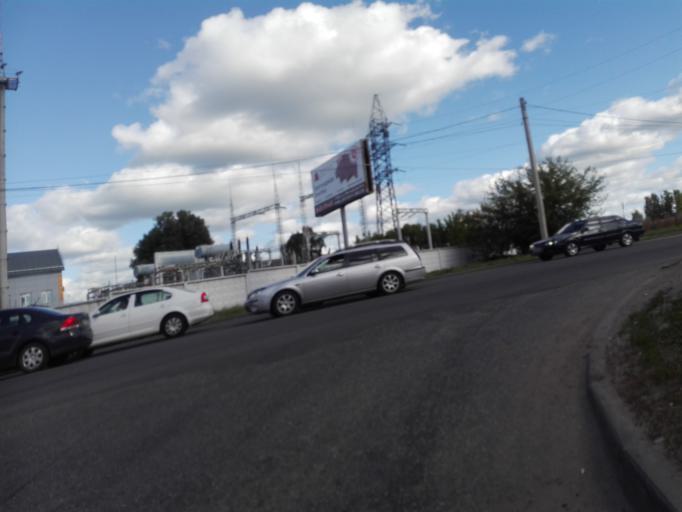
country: RU
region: Orjol
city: Orel
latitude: 52.9463
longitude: 36.0320
